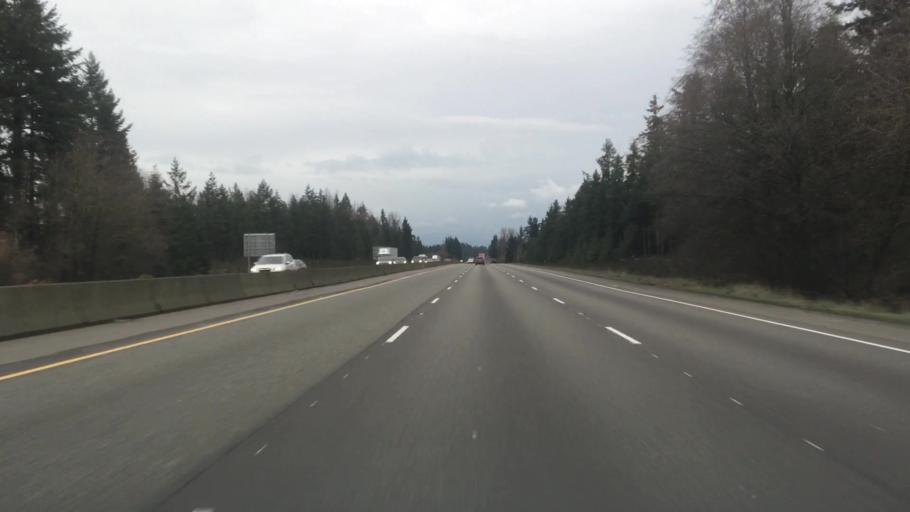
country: US
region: Washington
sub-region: Thurston County
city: Tumwater
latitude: 46.9368
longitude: -122.9423
